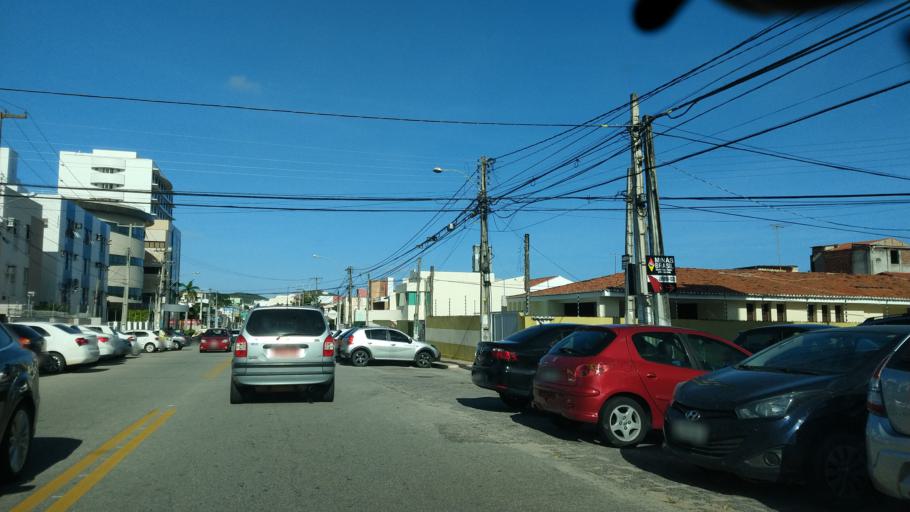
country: BR
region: Rio Grande do Norte
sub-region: Natal
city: Natal
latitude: -5.8242
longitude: -35.2080
